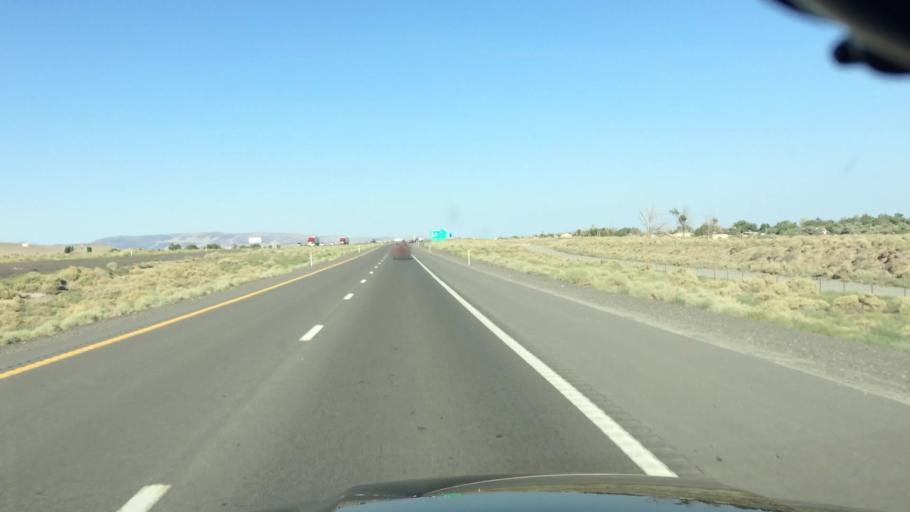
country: US
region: Nevada
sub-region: Lyon County
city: Fernley
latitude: 39.6151
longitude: -119.2471
